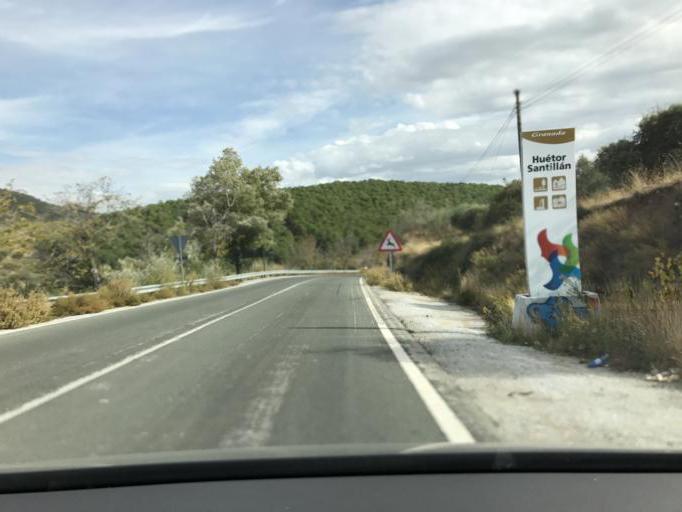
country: ES
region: Andalusia
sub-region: Provincia de Granada
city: Huetor Santillan
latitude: 37.2249
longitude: -3.5324
